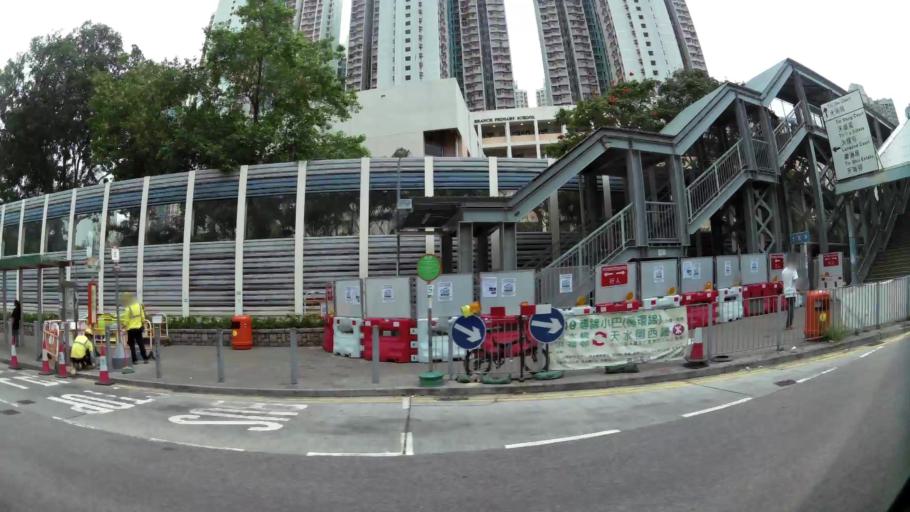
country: HK
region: Yuen Long
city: Yuen Long Kau Hui
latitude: 22.4470
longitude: 114.0030
